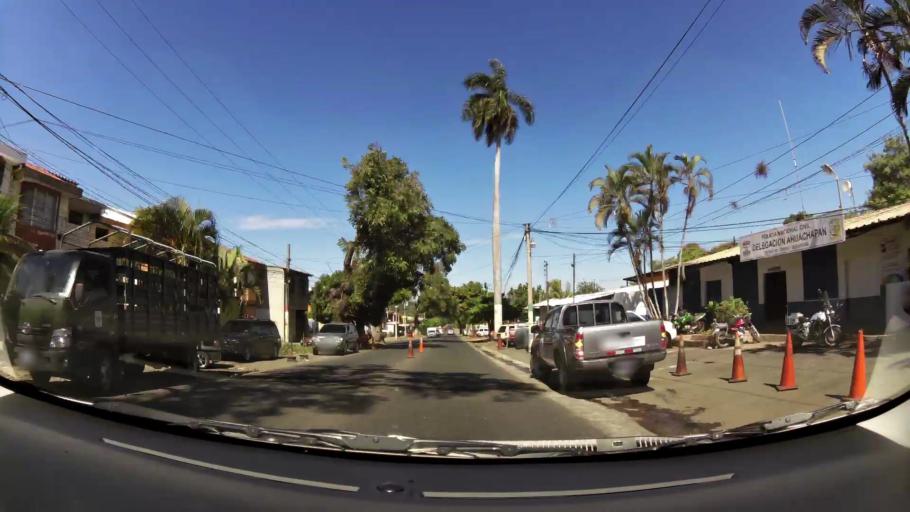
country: SV
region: Ahuachapan
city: Ahuachapan
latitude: 13.9276
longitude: -89.8517
